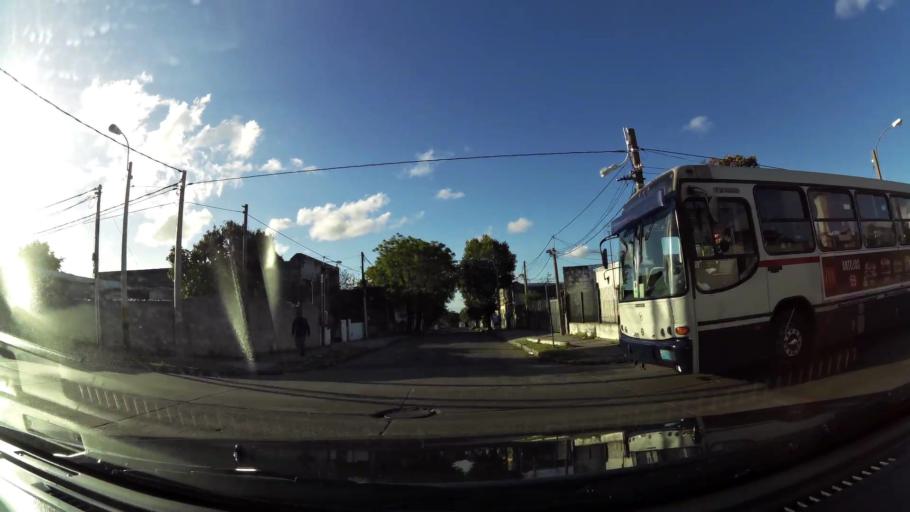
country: UY
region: Montevideo
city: Montevideo
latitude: -34.8726
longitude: -56.1441
